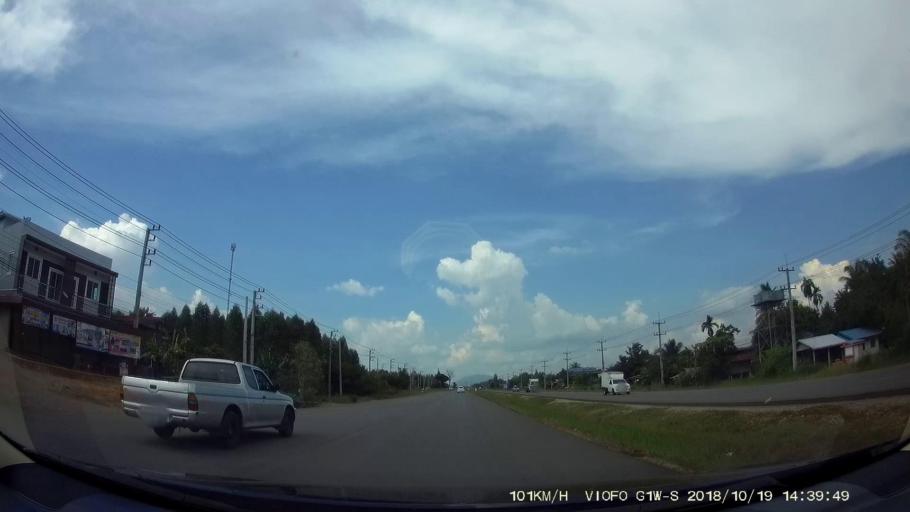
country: TH
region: Chaiyaphum
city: Kaeng Khro
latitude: 16.2315
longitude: 102.1948
